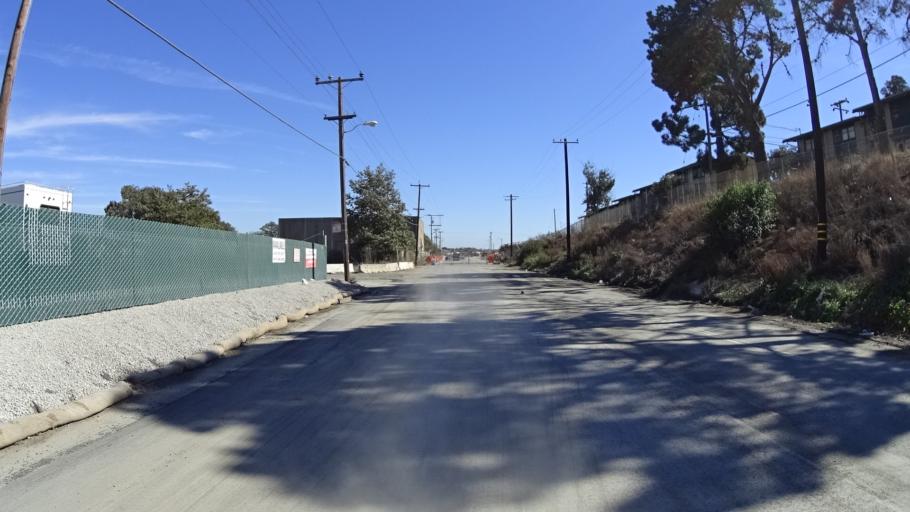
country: US
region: California
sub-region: San Mateo County
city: Brisbane
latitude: 37.7209
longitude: -122.3861
